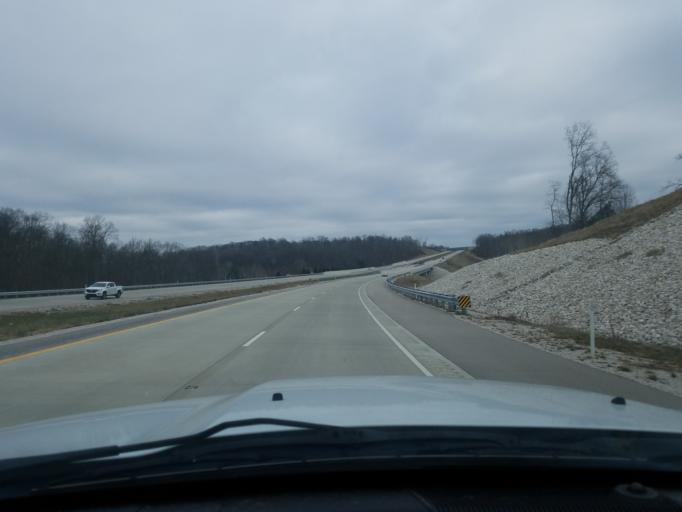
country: US
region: Indiana
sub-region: Monroe County
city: Ellettsville
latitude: 39.0668
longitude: -86.6777
